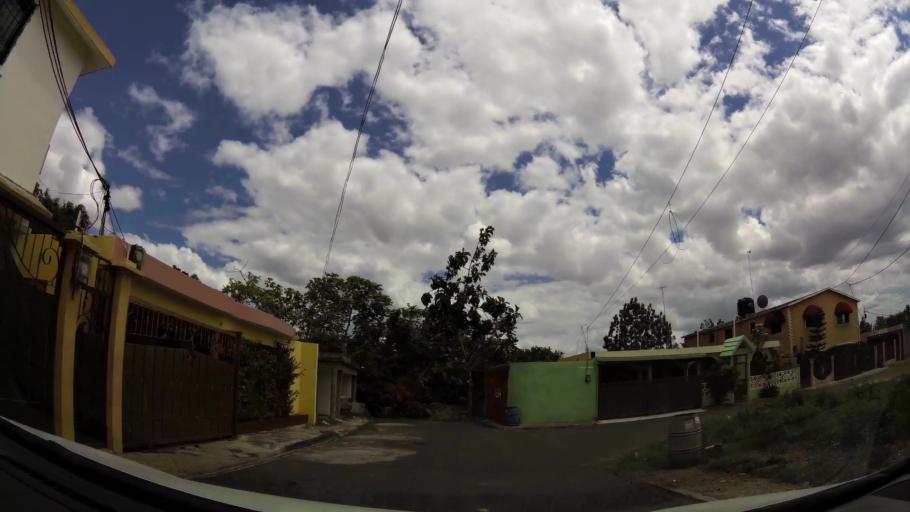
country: DO
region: Nacional
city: Ensanche Luperon
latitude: 18.5211
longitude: -69.9071
